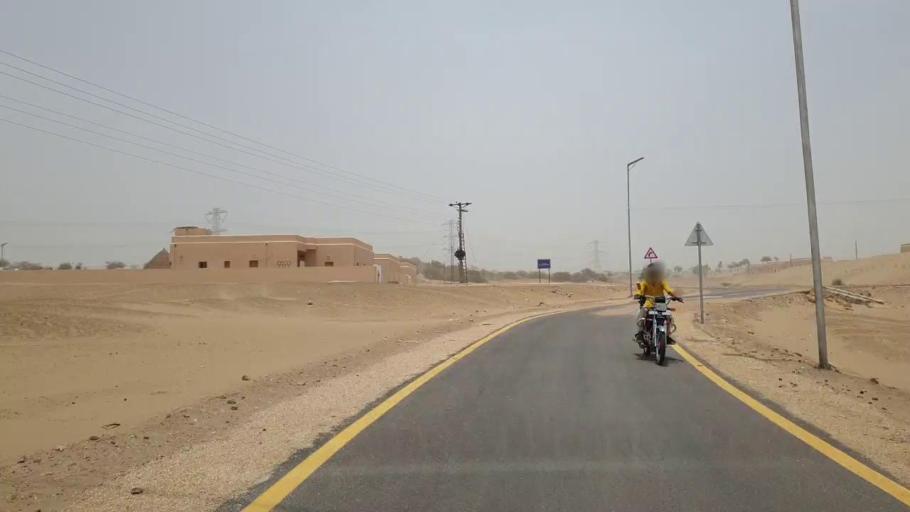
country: PK
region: Sindh
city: Islamkot
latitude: 24.7233
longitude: 70.3266
